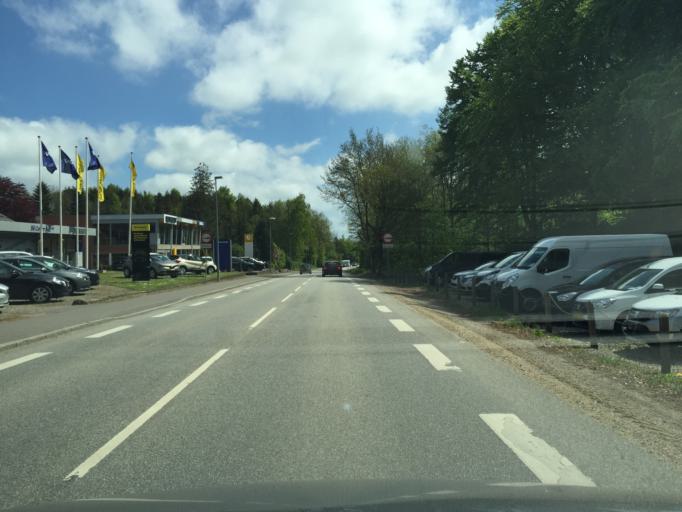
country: DK
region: Zealand
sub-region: Vordingborg Kommune
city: Nyrad
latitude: 54.9967
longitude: 12.0123
